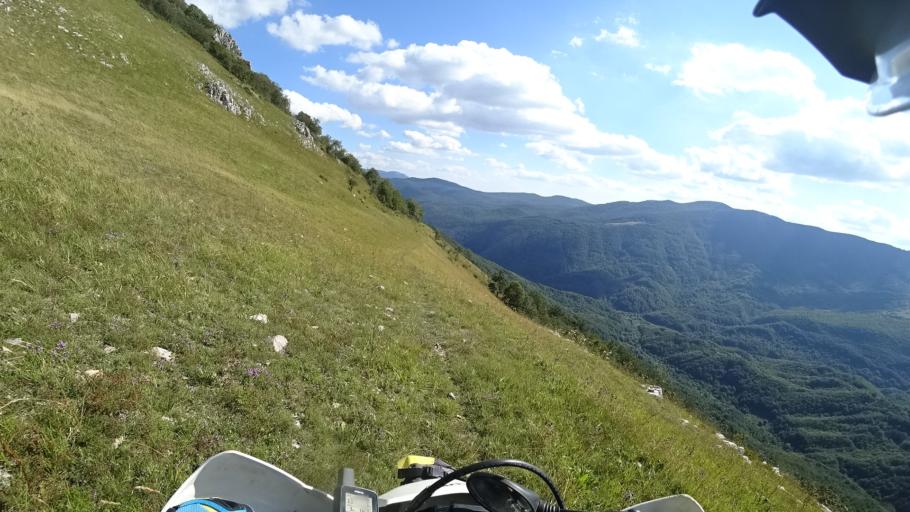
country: HR
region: Zadarska
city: Gracac
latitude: 44.3827
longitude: 16.0463
